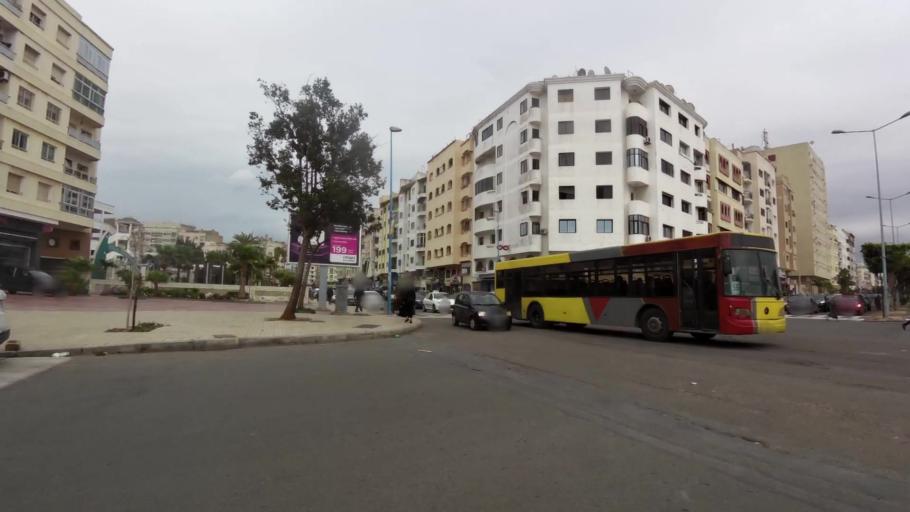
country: MA
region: Grand Casablanca
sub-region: Casablanca
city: Casablanca
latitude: 33.5964
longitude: -7.6480
